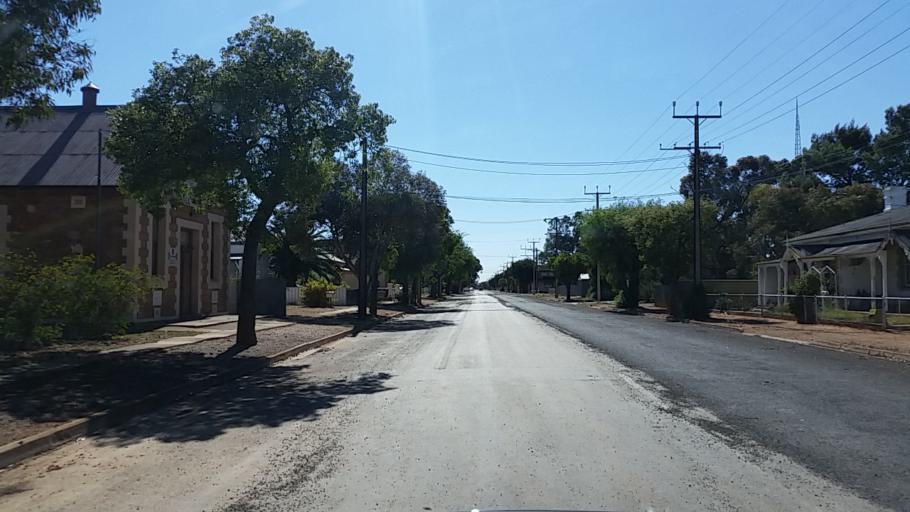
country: AU
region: South Australia
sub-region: Peterborough
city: Peterborough
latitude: -32.9723
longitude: 138.8364
